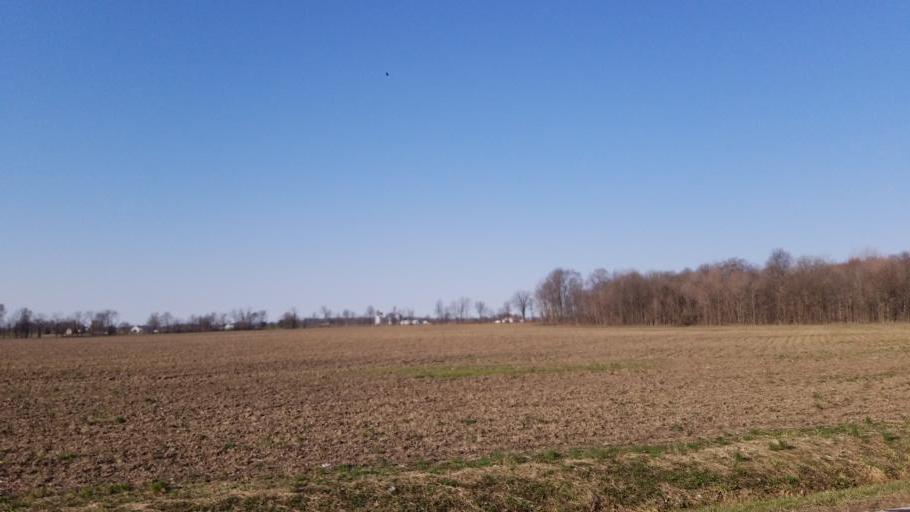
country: US
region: Ohio
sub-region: Morrow County
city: Mount Gilead
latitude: 40.5630
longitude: -82.8753
